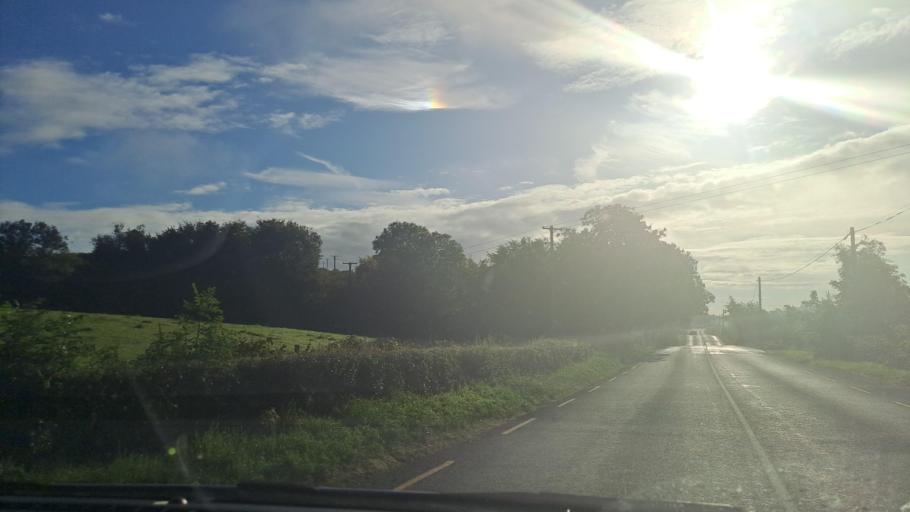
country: IE
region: Ulster
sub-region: County Monaghan
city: Carrickmacross
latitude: 53.9978
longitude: -6.7940
